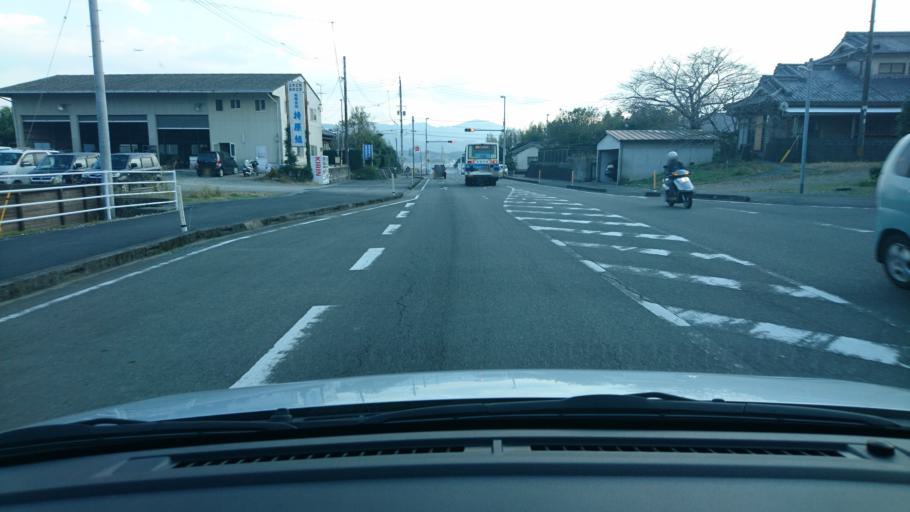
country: JP
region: Miyazaki
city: Miyazaki-shi
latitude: 31.8616
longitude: 131.3995
